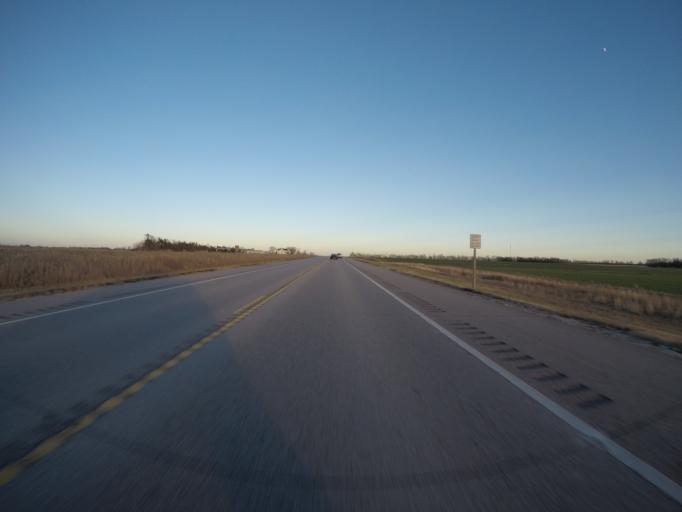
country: US
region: Kansas
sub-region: Marion County
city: Peabody
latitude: 38.1747
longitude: -97.1513
